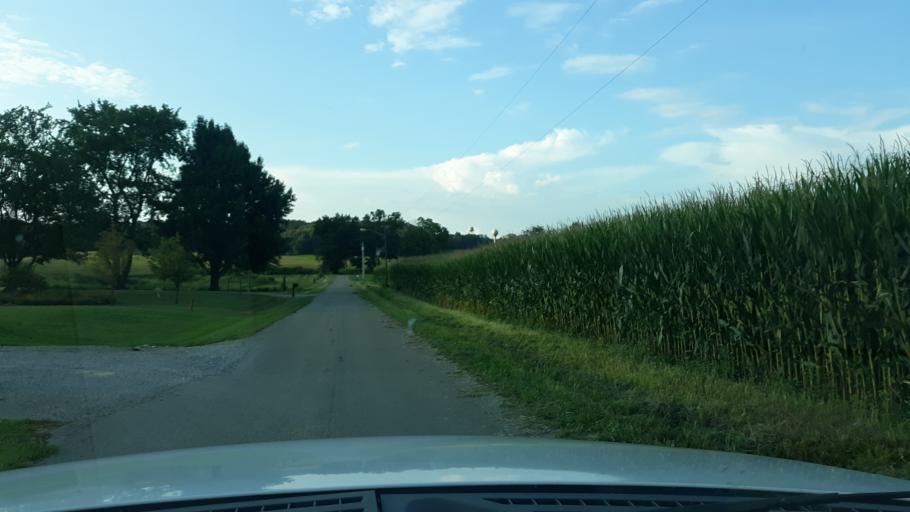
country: US
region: Illinois
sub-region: Saline County
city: Eldorado
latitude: 37.8321
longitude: -88.5165
